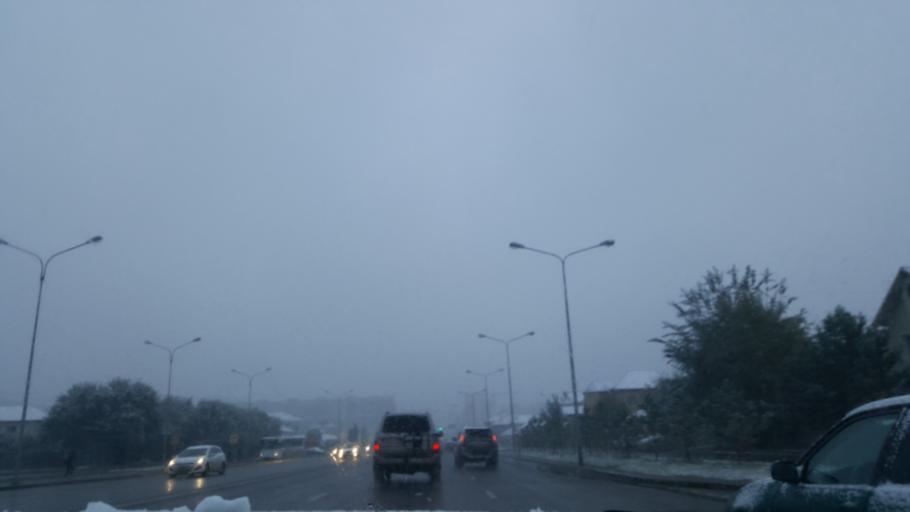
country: KZ
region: Astana Qalasy
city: Astana
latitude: 51.1362
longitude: 71.4920
